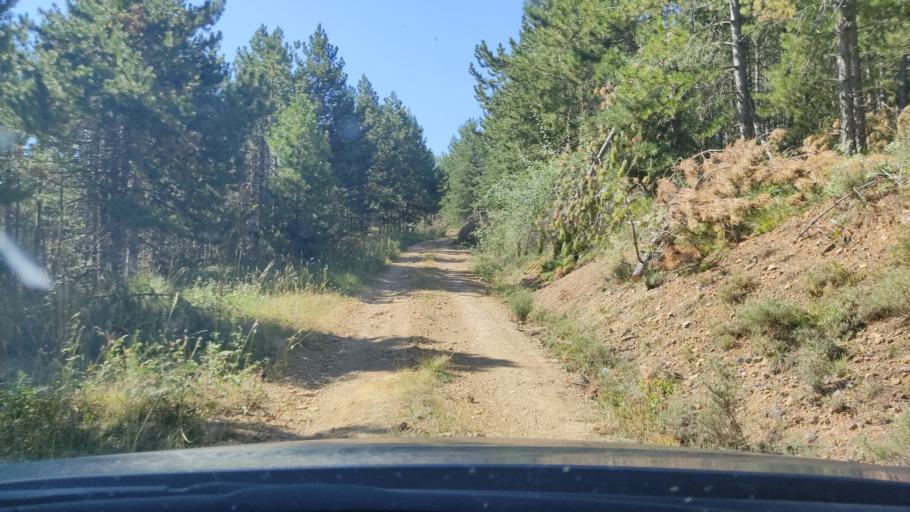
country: ES
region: Aragon
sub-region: Provincia de Teruel
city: Monforte de Moyuela
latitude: 41.0362
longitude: -1.0426
